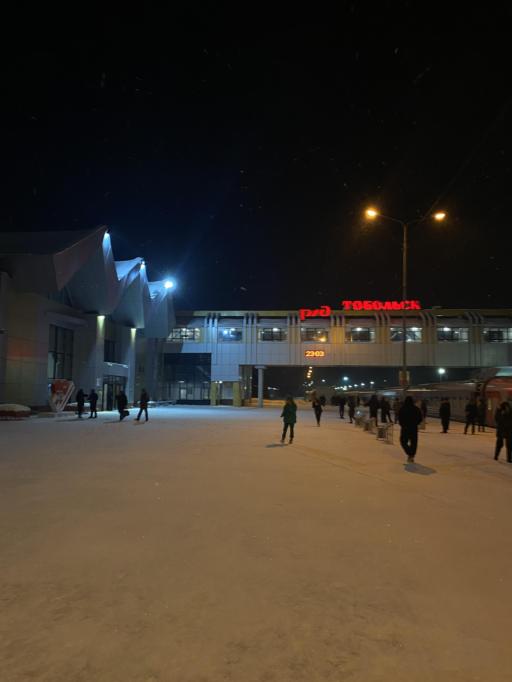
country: RU
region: Tjumen
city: Tobol'sk
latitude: 58.2887
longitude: 68.3113
